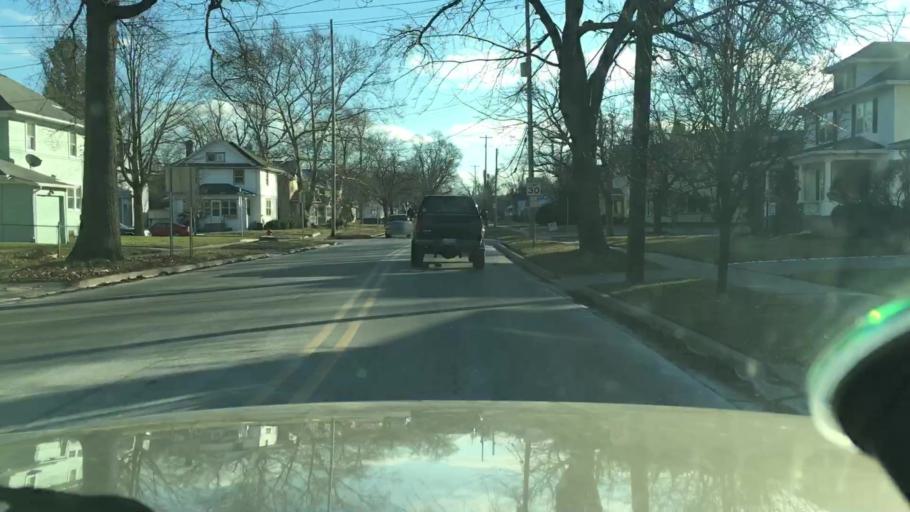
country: US
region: Michigan
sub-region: Jackson County
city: Jackson
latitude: 42.2397
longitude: -84.4234
